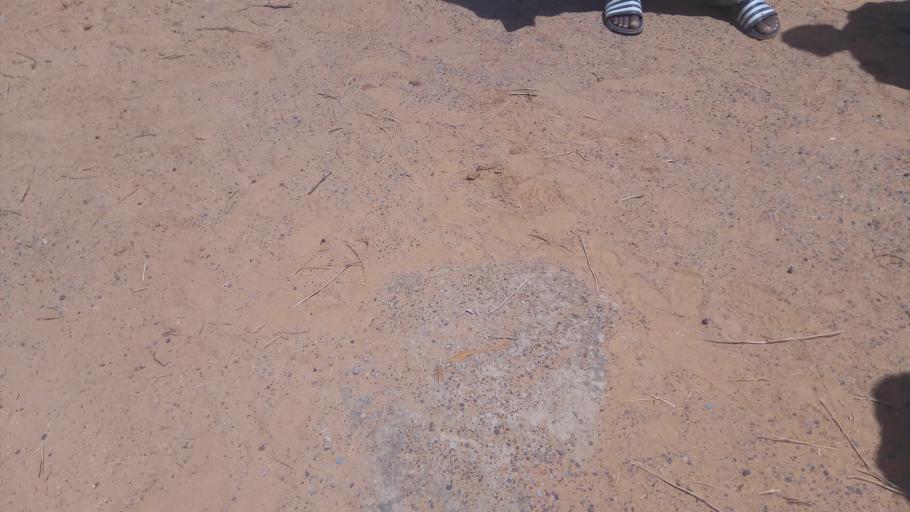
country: ML
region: Kayes
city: Diema
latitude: 14.5096
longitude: -8.8415
